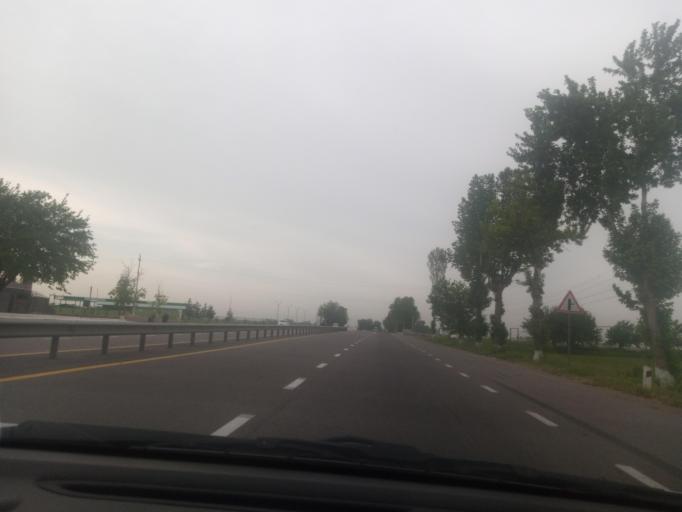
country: UZ
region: Toshkent Shahri
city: Bektemir
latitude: 41.1492
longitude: 69.4283
